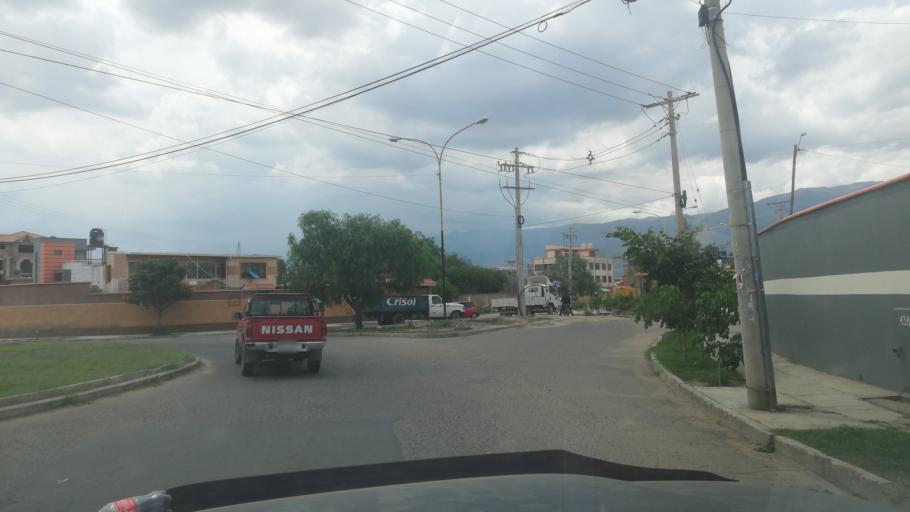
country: BO
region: Cochabamba
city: Cochabamba
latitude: -17.4024
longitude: -66.1796
